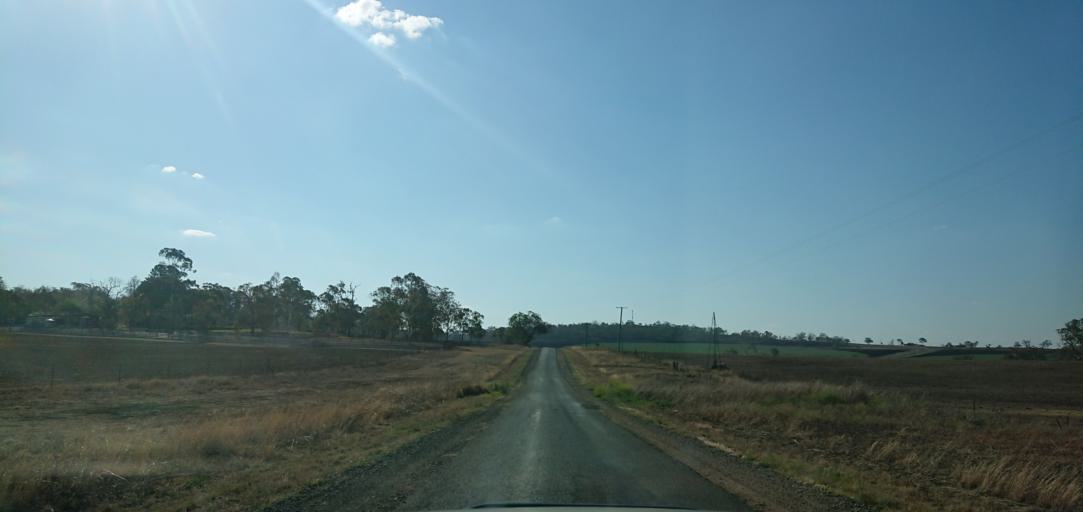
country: AU
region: Queensland
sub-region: Toowoomba
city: Westbrook
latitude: -27.7138
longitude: 151.7182
